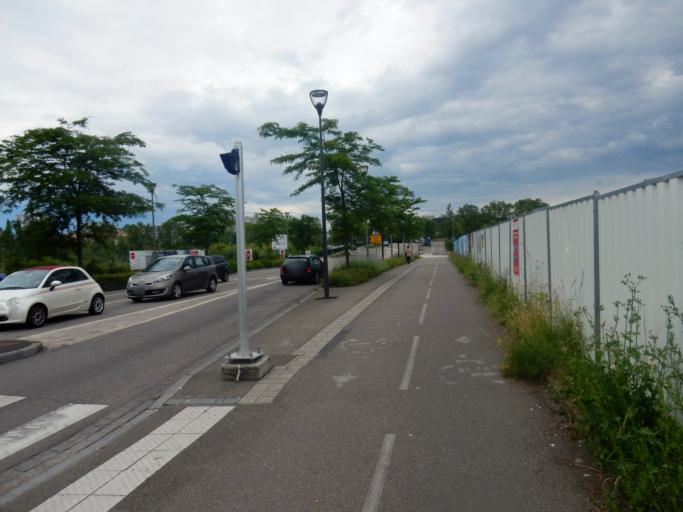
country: FR
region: Alsace
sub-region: Departement du Bas-Rhin
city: Strasbourg
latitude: 48.5717
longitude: 7.7705
